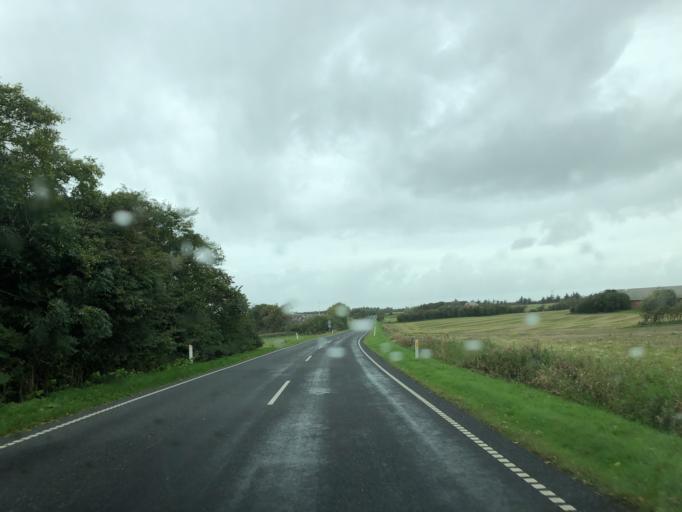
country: DK
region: North Denmark
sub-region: Thisted Kommune
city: Hurup
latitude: 56.7223
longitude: 8.3513
